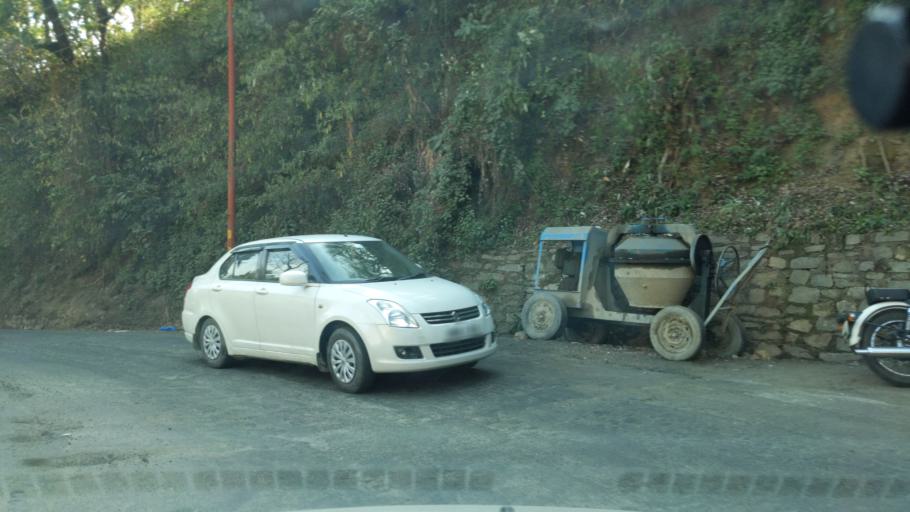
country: IN
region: Uttarakhand
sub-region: Naini Tal
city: Bhowali
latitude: 29.3912
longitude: 79.5309
